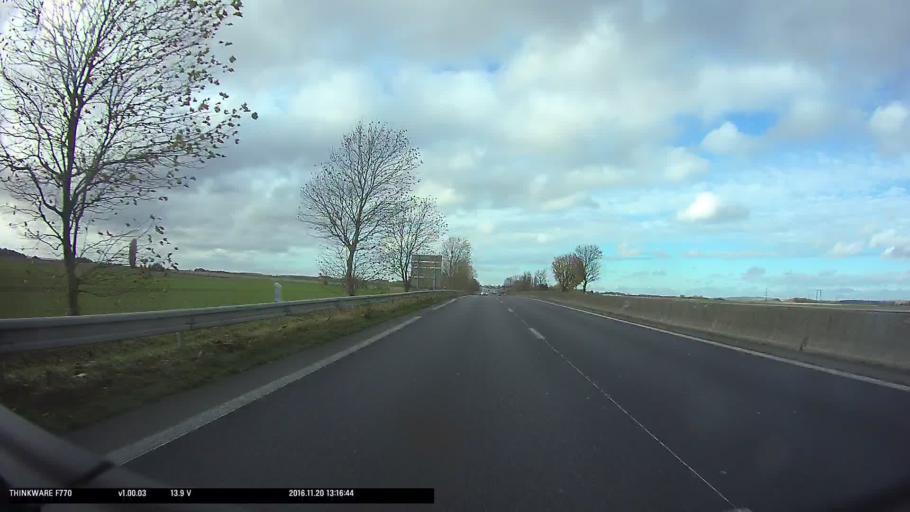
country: FR
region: Ile-de-France
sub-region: Departement du Val-d'Oise
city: Courdimanche
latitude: 49.0618
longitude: 1.9903
